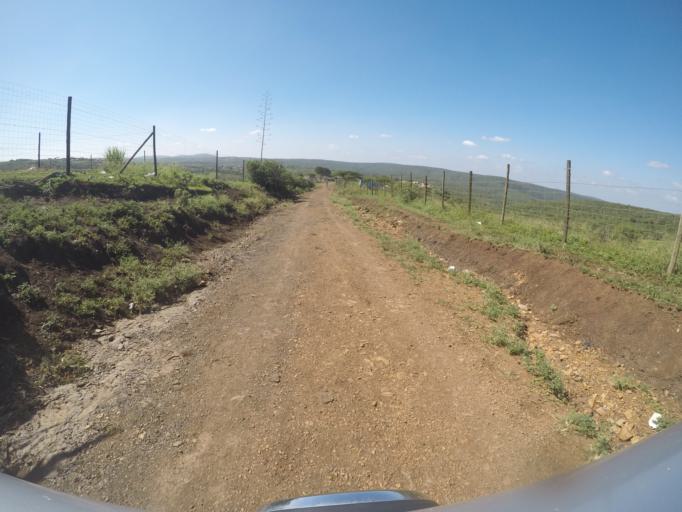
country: ZA
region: KwaZulu-Natal
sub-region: uThungulu District Municipality
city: Empangeni
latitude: -28.5615
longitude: 31.7036
